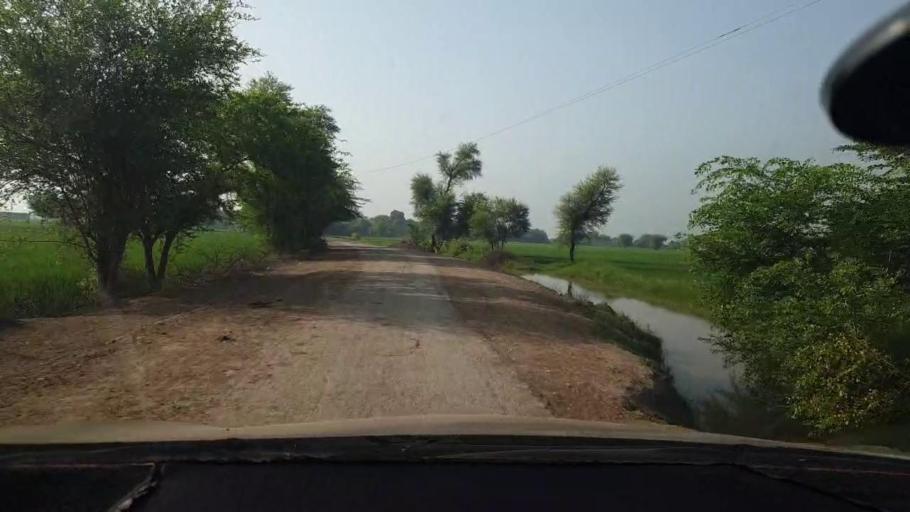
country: PK
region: Sindh
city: Kambar
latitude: 27.5376
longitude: 68.0182
